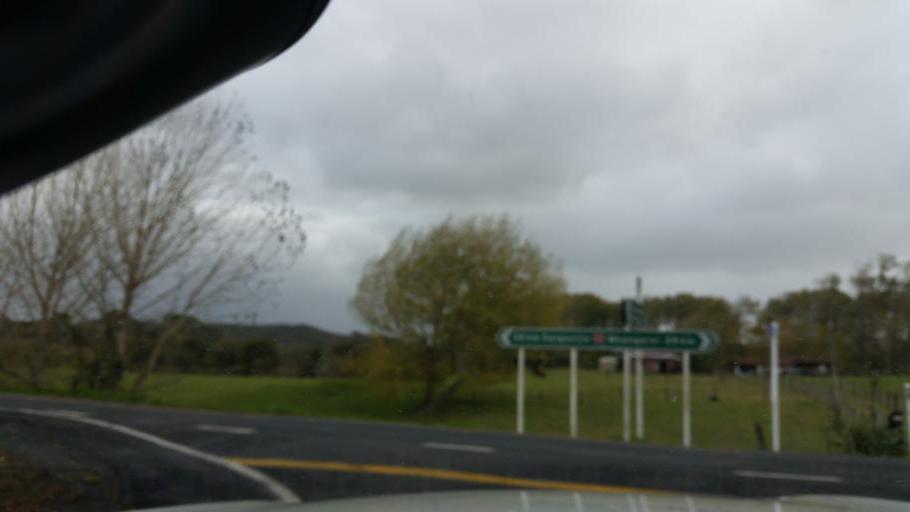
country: NZ
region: Northland
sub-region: Whangarei
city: Maungatapere
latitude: -35.8215
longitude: 174.0446
